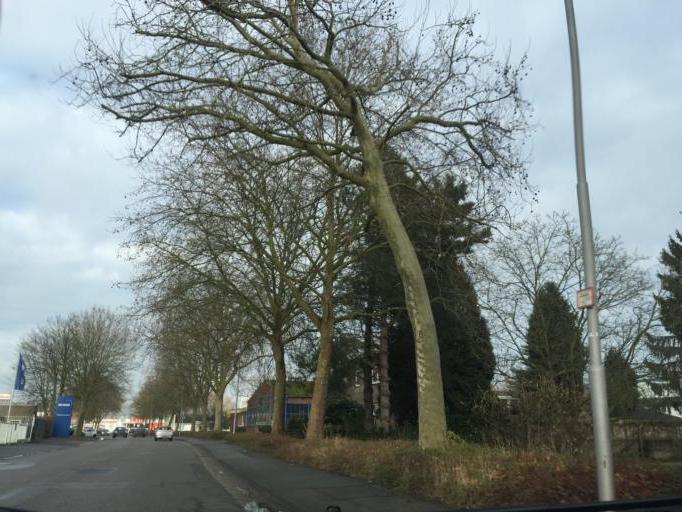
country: DE
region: North Rhine-Westphalia
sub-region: Regierungsbezirk Dusseldorf
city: Kleve
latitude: 51.7971
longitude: 6.1397
